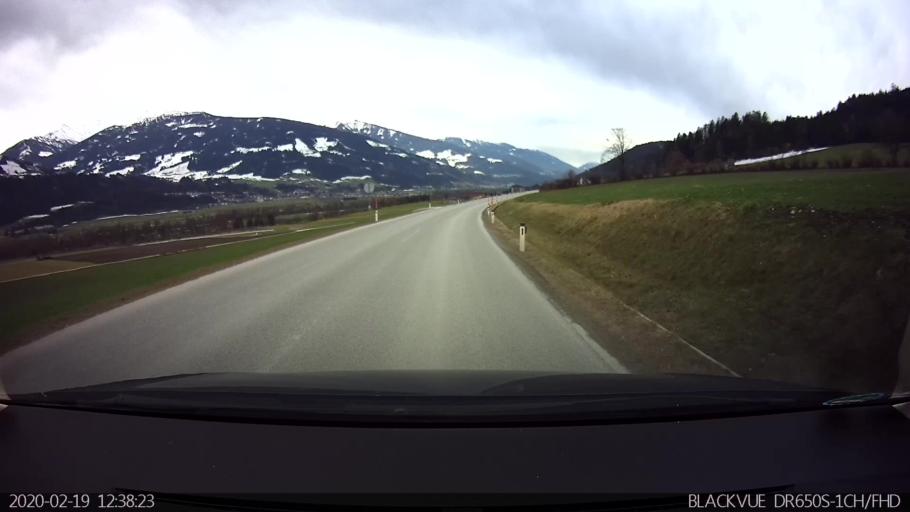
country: AT
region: Tyrol
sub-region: Politischer Bezirk Schwaz
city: Terfens
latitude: 47.3286
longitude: 11.6541
